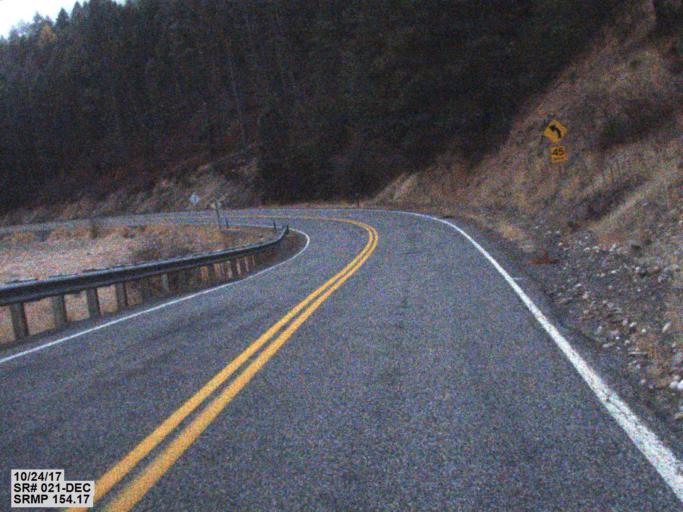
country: US
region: Washington
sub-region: Ferry County
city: Republic
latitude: 48.5595
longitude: -118.7440
